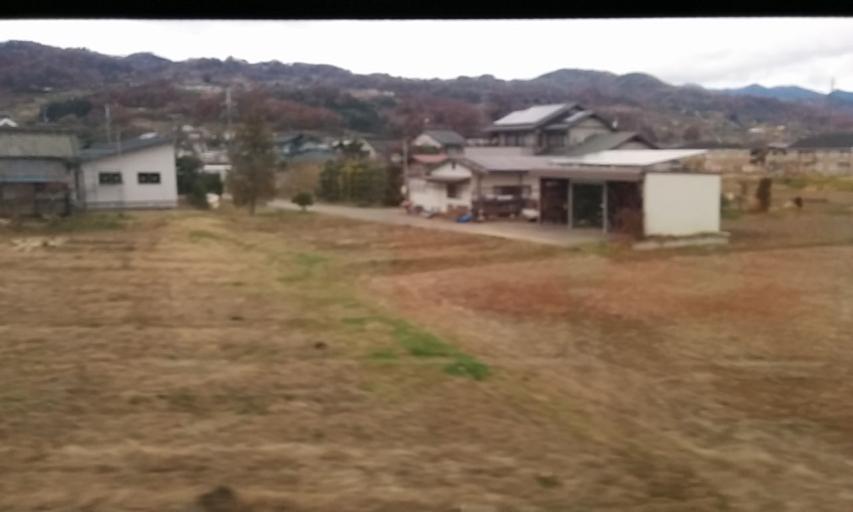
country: JP
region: Nagano
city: Nagano-shi
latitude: 36.5686
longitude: 138.1301
